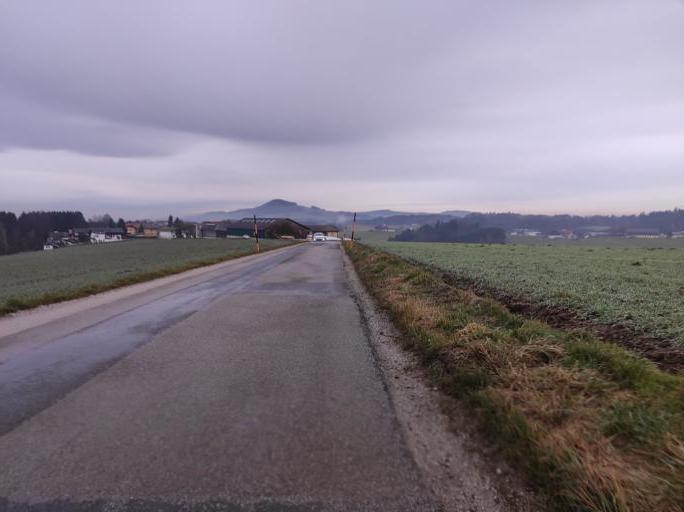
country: AT
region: Salzburg
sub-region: Politischer Bezirk Salzburg-Umgebung
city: Obertrum am See
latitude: 47.9098
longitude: 13.0680
